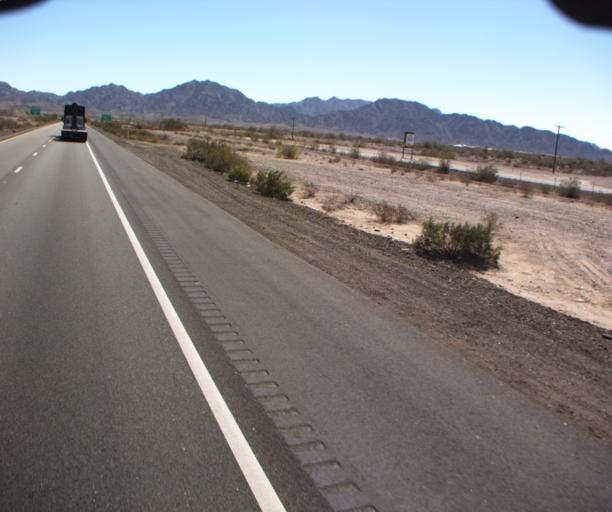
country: US
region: Arizona
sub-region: Yuma County
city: Fortuna Foothills
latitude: 32.6641
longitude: -114.3876
